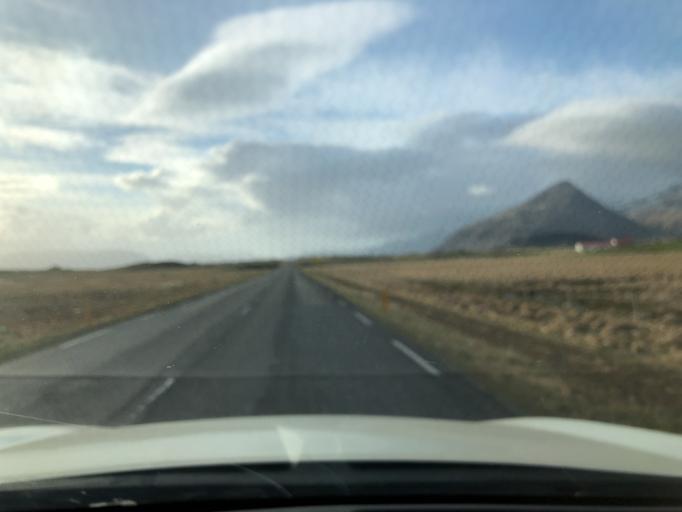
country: IS
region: East
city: Hoefn
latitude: 64.2943
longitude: -15.1888
